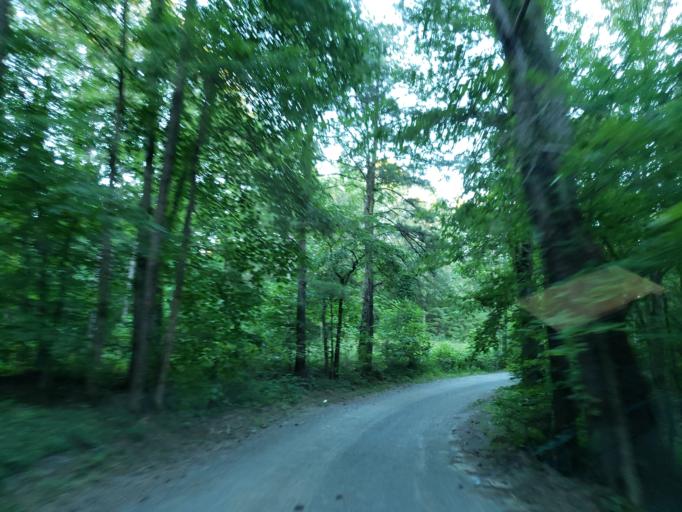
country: US
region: Georgia
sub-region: Bartow County
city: Euharlee
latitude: 34.0871
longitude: -84.8668
